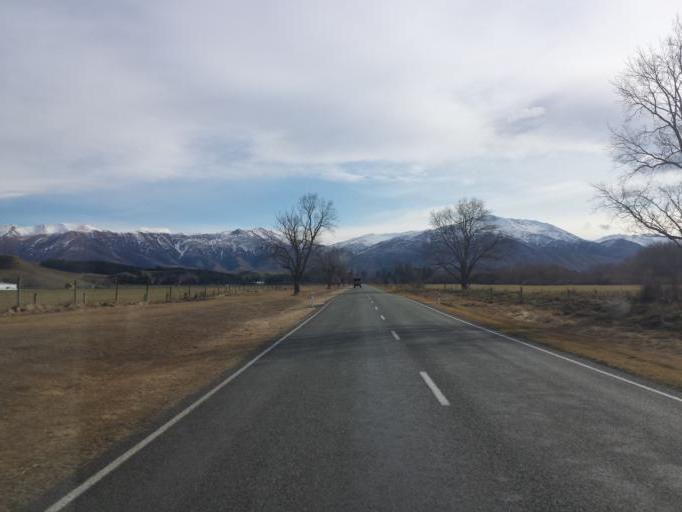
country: NZ
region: Canterbury
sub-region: Timaru District
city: Pleasant Point
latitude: -44.0570
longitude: 170.7727
